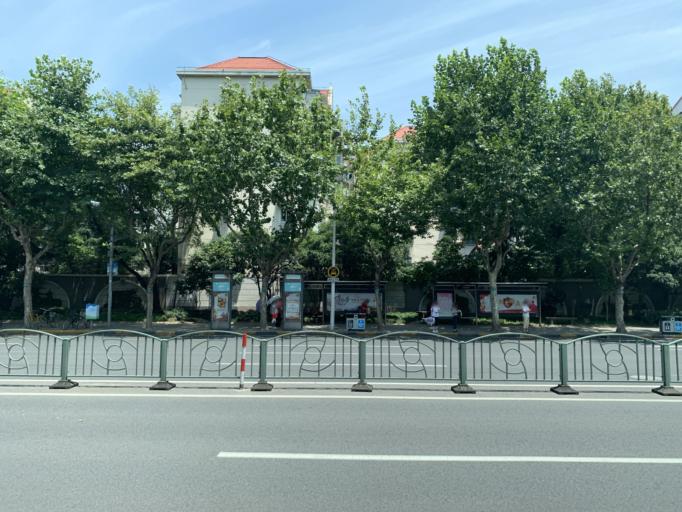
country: CN
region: Shanghai Shi
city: Pudong
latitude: 31.2365
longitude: 121.5182
